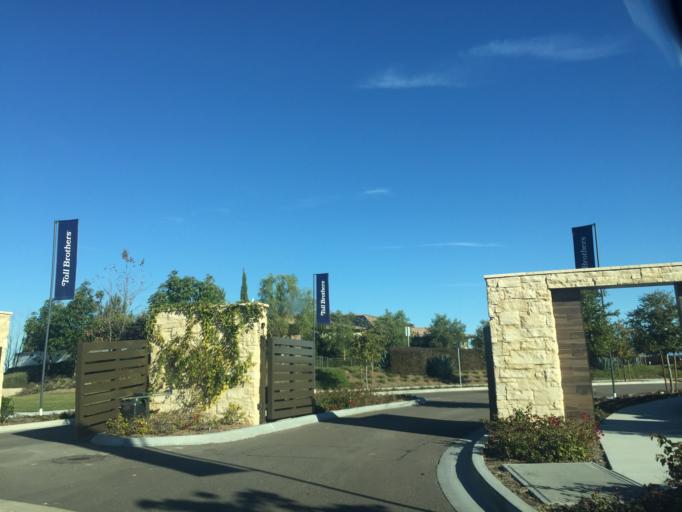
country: US
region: California
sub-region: San Diego County
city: Fairbanks Ranch
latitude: 32.9703
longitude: -117.1933
